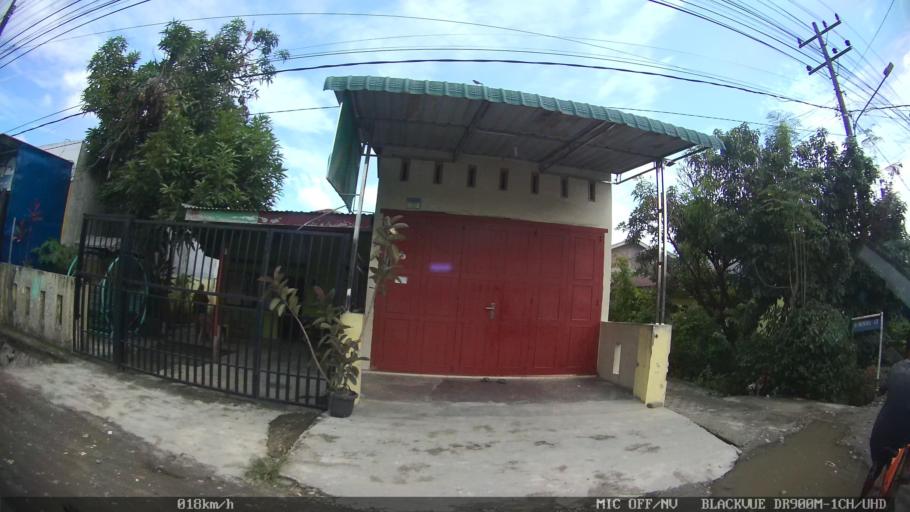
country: ID
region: North Sumatra
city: Percut
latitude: 3.6021
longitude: 98.7671
